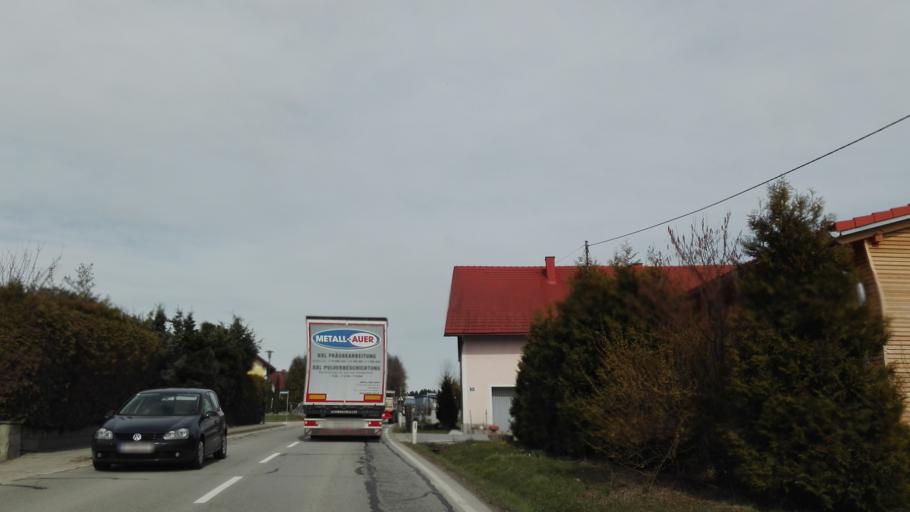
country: AT
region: Upper Austria
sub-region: Politischer Bezirk Scharding
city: Scharding
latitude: 48.4711
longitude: 13.4464
